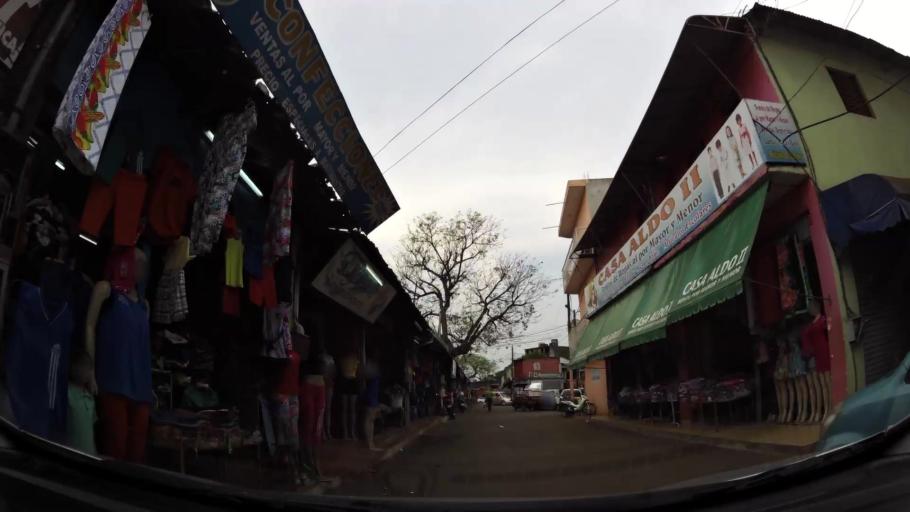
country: PY
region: Alto Parana
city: Presidente Franco
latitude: -25.5339
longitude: -54.6125
